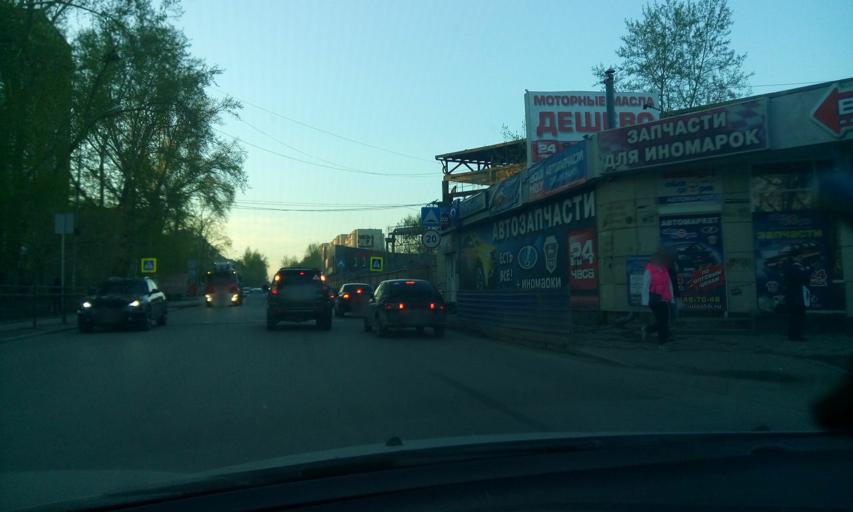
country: RU
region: Sverdlovsk
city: Yekaterinburg
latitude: 56.8280
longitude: 60.6935
